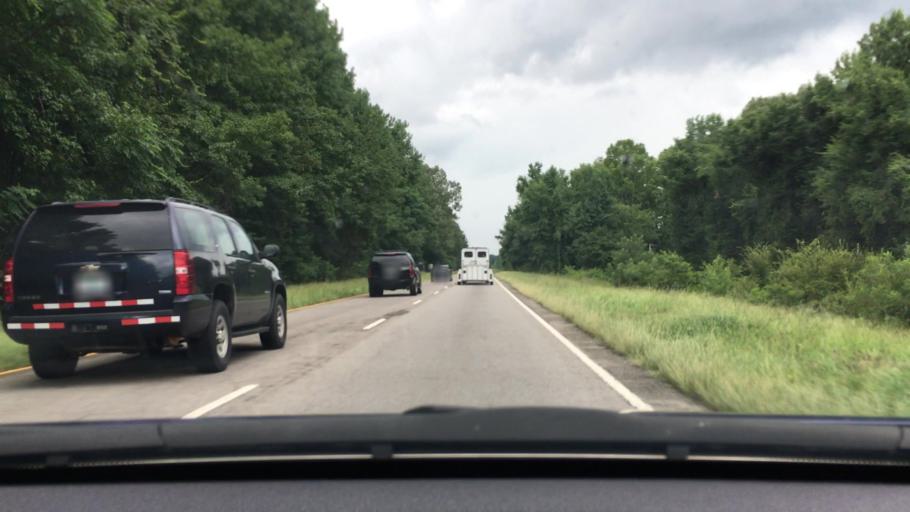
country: US
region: South Carolina
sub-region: Sumter County
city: Stateburg
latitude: 33.9479
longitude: -80.6178
